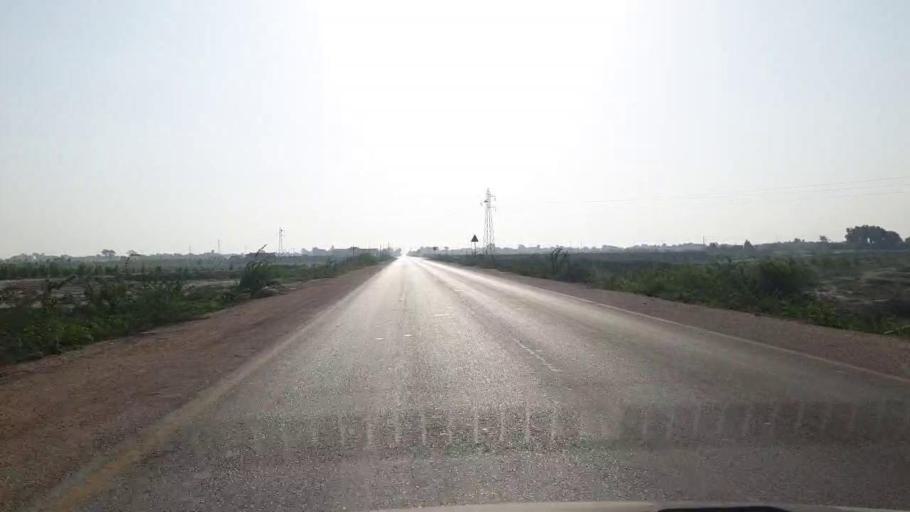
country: PK
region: Sindh
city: Badin
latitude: 24.6798
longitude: 68.8421
